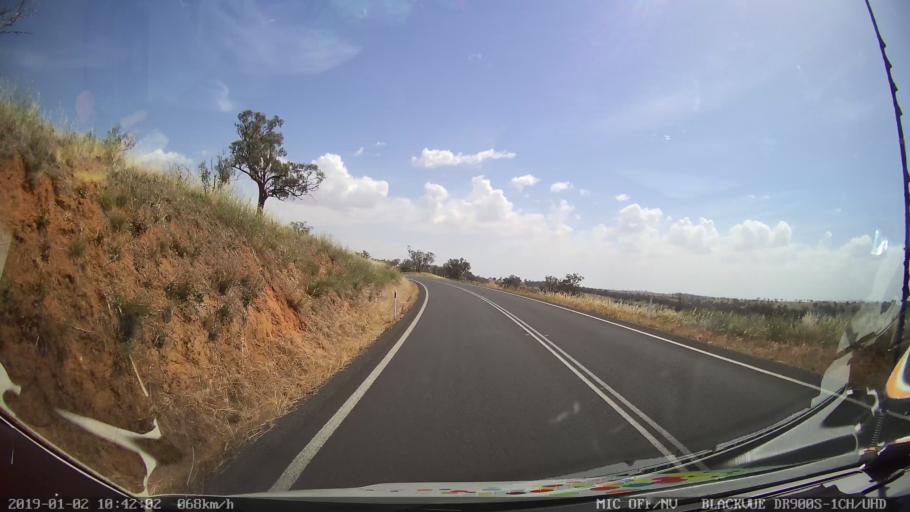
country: AU
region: New South Wales
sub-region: Cootamundra
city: Cootamundra
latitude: -34.7891
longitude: 148.3086
